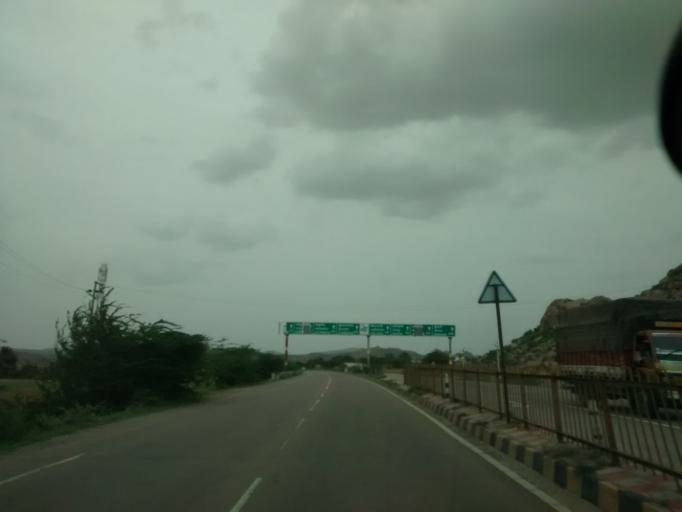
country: IN
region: Andhra Pradesh
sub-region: Kurnool
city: Ramapuram
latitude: 15.1675
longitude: 77.6790
